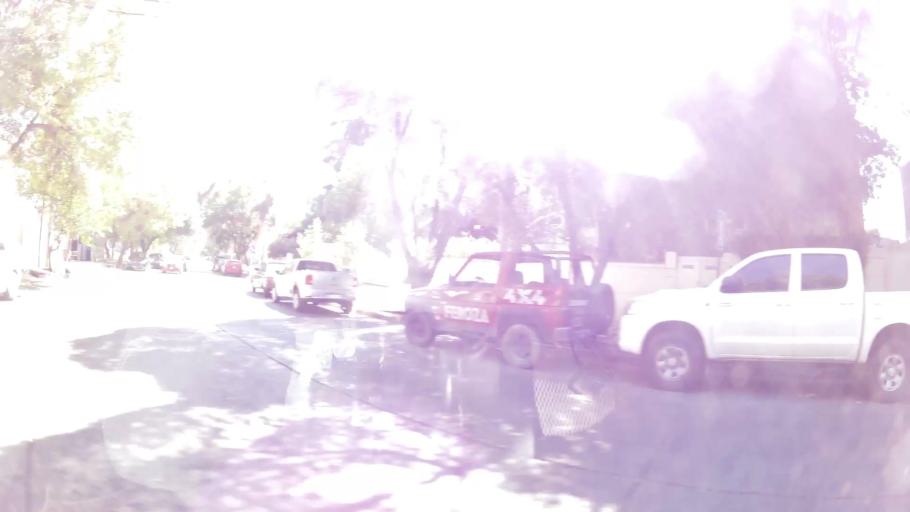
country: AR
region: Mendoza
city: Mendoza
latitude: -32.9028
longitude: -68.8572
